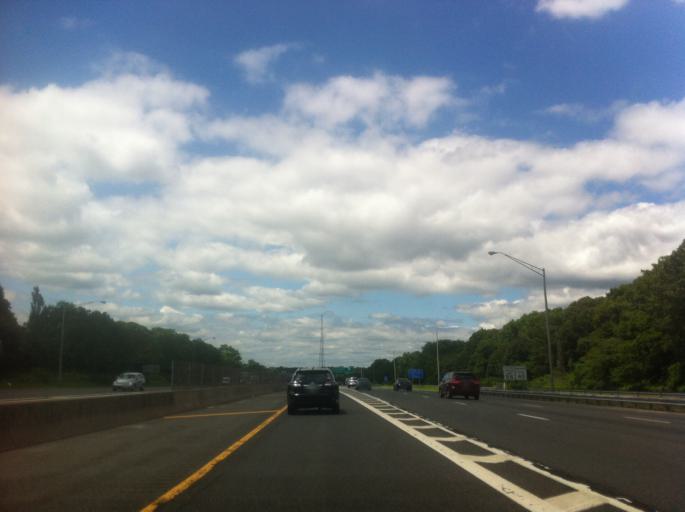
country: US
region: New York
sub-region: Suffolk County
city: Hauppauge
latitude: 40.8093
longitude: -73.2070
